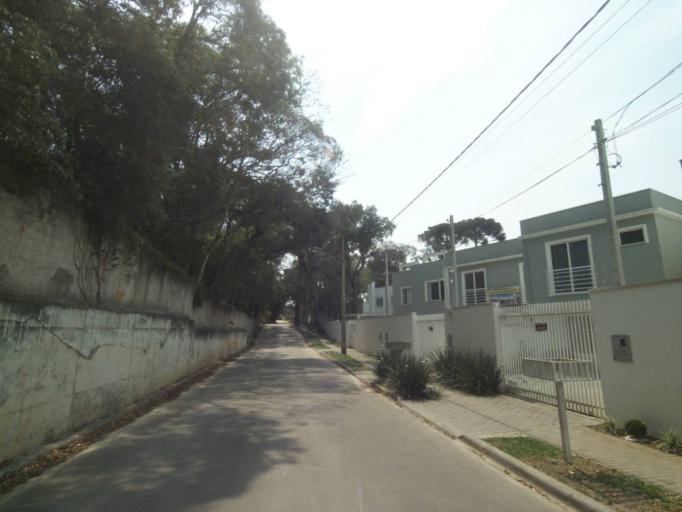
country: BR
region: Parana
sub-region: Pinhais
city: Pinhais
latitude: -25.4840
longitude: -49.2109
